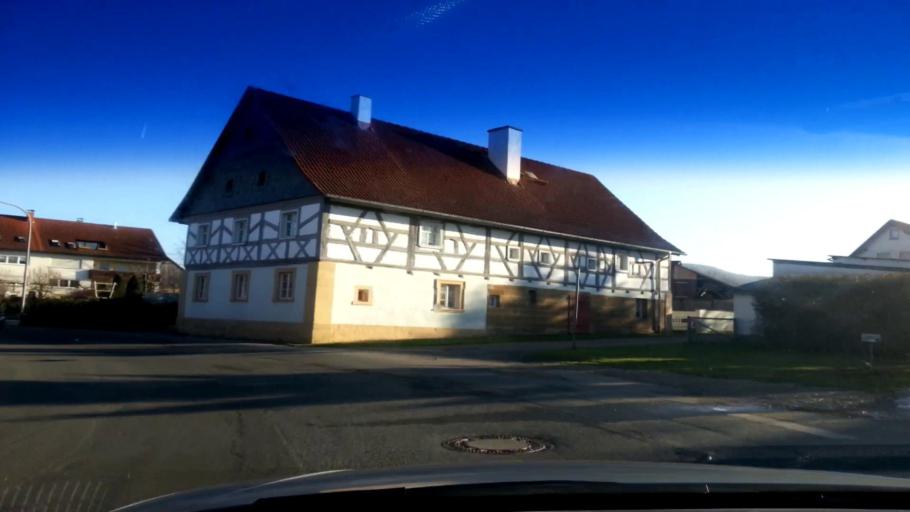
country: DE
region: Bavaria
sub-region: Upper Franconia
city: Schesslitz
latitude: 49.9554
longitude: 11.0182
